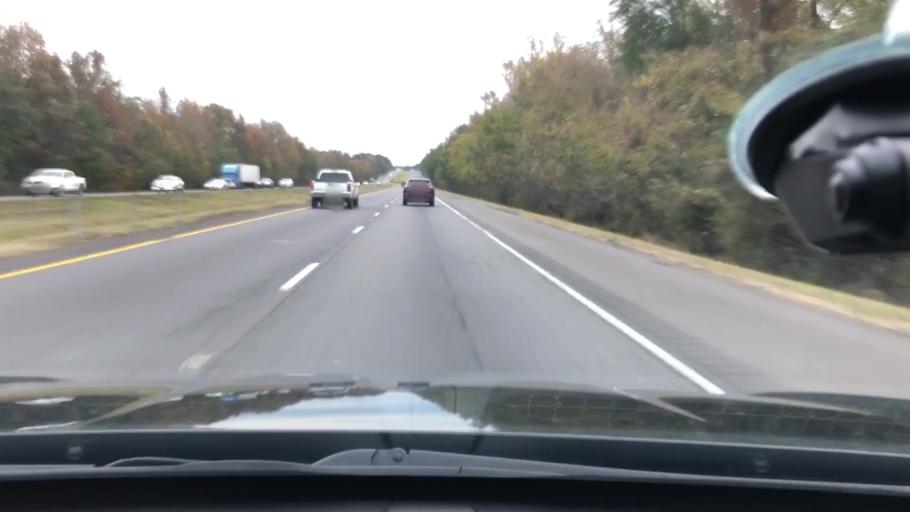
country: US
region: Arkansas
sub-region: Clark County
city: Gurdon
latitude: 34.0229
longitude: -93.1568
